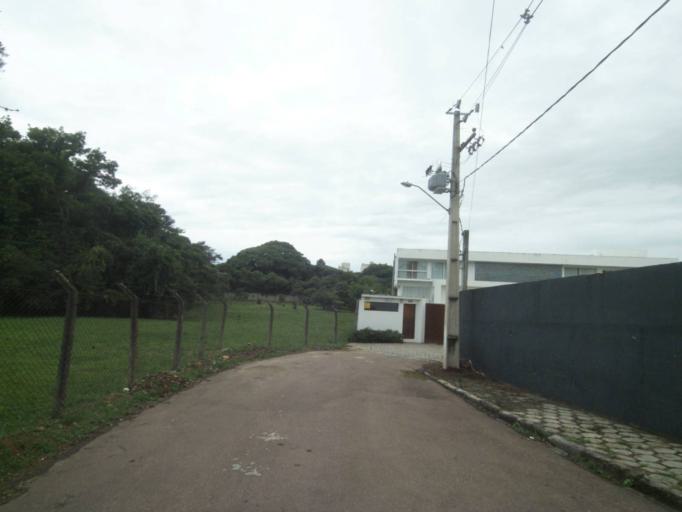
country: BR
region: Parana
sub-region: Curitiba
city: Curitiba
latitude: -25.4532
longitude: -49.3137
